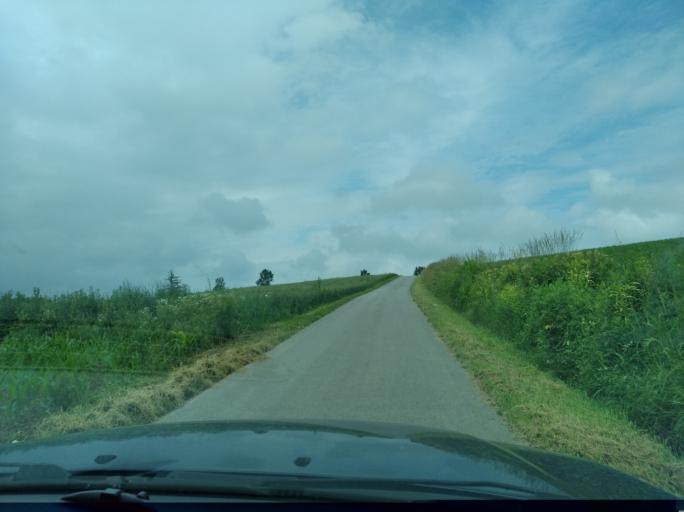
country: PL
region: Subcarpathian Voivodeship
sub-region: Powiat jaroslawski
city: Pruchnik
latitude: 49.9047
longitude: 22.4984
